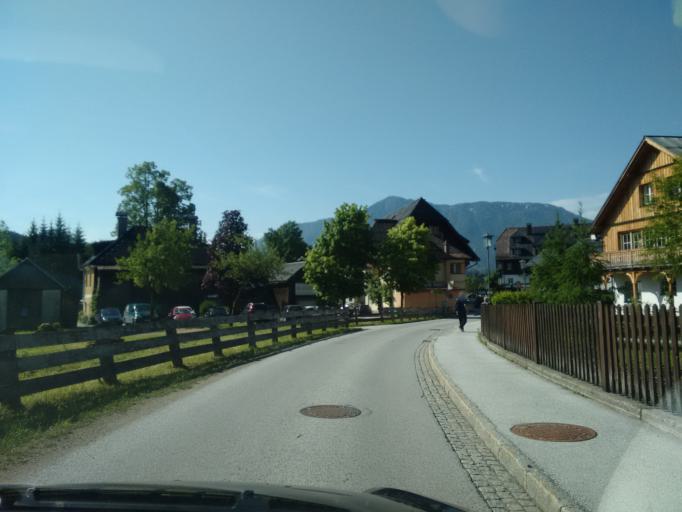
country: AT
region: Styria
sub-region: Politischer Bezirk Liezen
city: Altaussee
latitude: 47.6403
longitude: 13.7633
